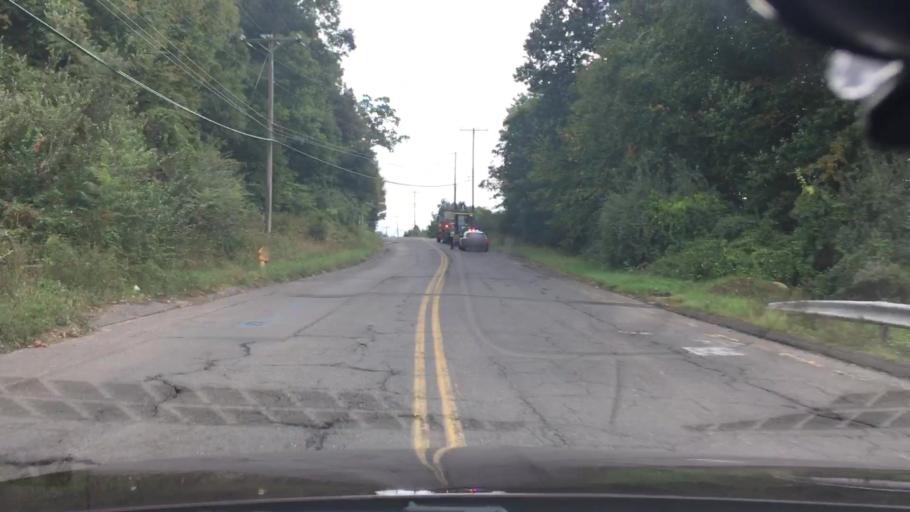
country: US
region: Connecticut
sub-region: New Haven County
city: Cheshire Village
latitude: 41.5548
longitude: -72.8990
